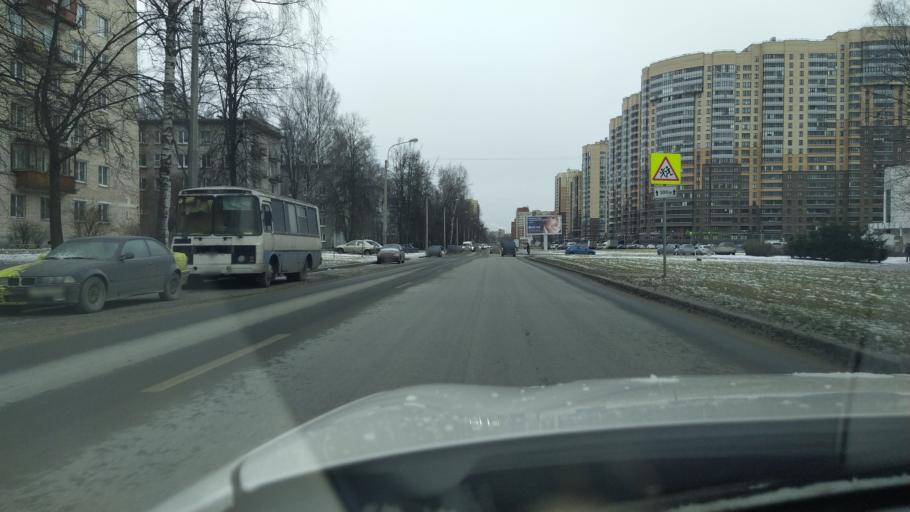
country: RU
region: Leningrad
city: Kalininskiy
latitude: 60.0011
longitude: 30.3959
